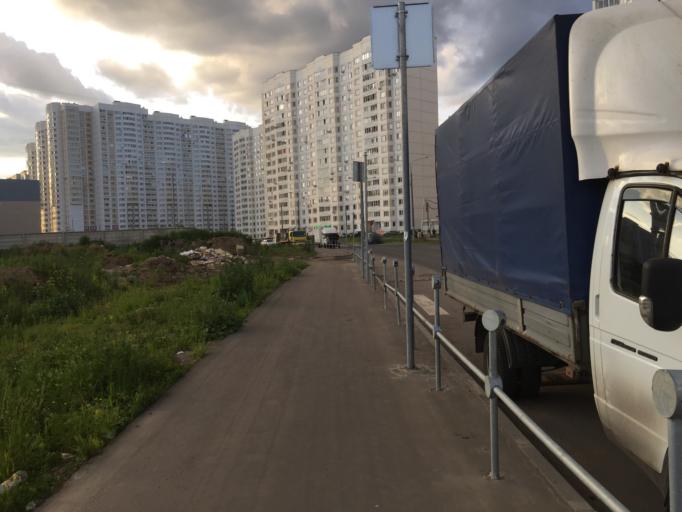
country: RU
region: Moscow
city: Nekrasovka
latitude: 55.6847
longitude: 37.9100
